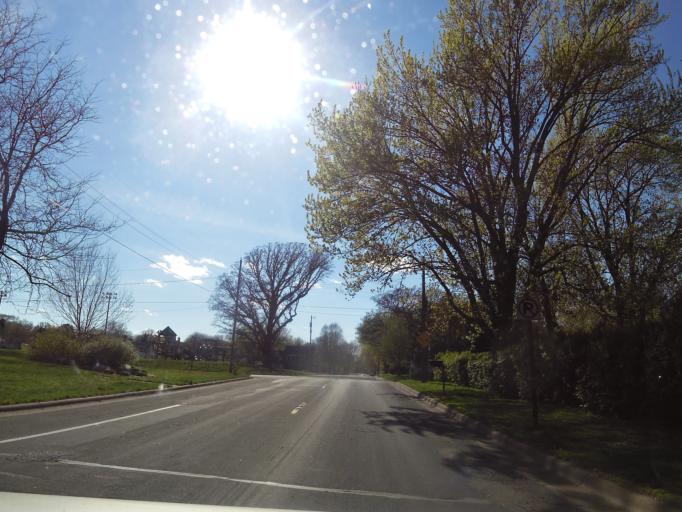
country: US
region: Minnesota
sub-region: Washington County
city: Stillwater
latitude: 45.0457
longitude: -92.8006
